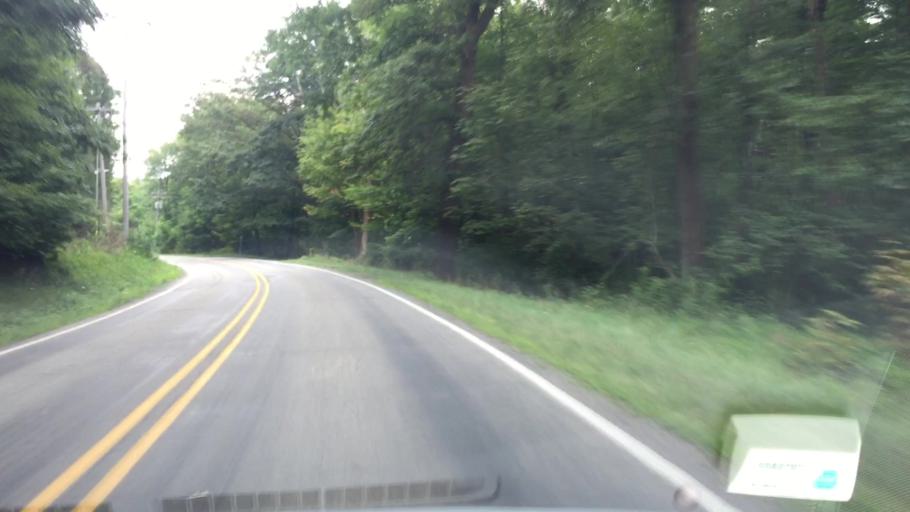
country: US
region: Pennsylvania
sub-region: Allegheny County
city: Curtisville
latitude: 40.7006
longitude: -79.8461
